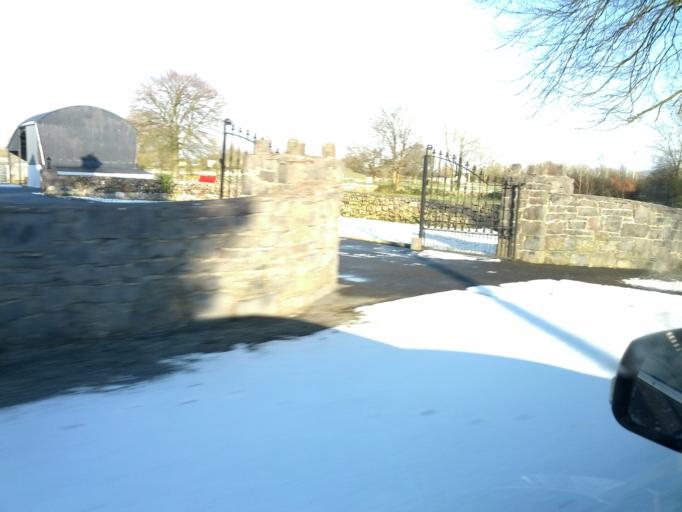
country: IE
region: Connaught
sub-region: County Galway
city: Gort
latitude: 53.1772
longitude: -8.7907
